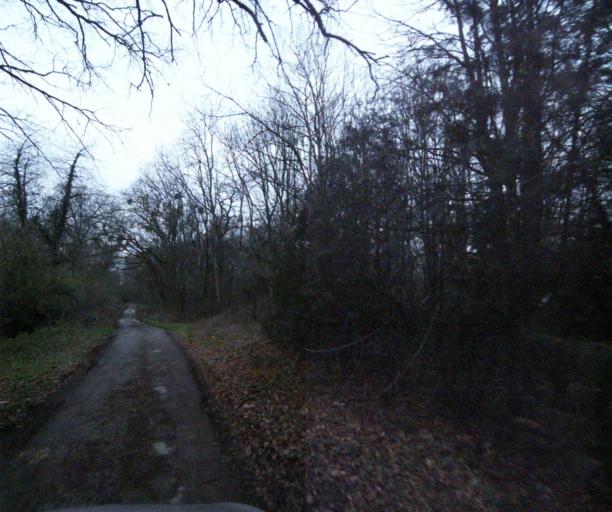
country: FR
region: Ile-de-France
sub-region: Departement de Seine-et-Marne
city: Longperrier
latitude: 49.0644
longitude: 2.6533
